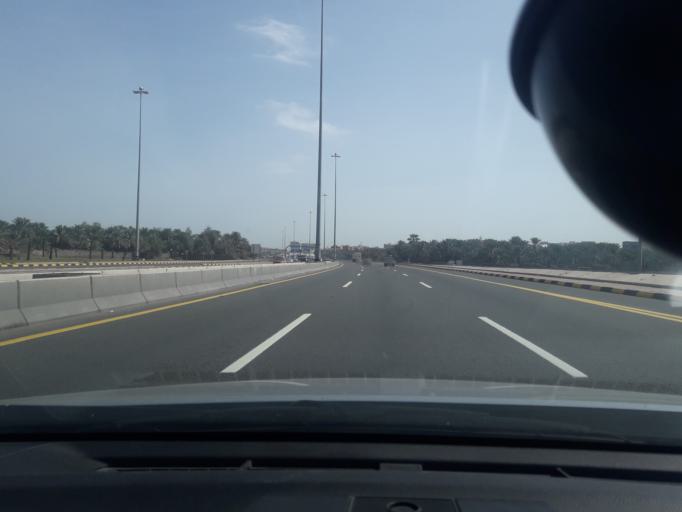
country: SA
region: Al Madinah al Munawwarah
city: Medina
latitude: 24.4412
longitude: 39.6289
